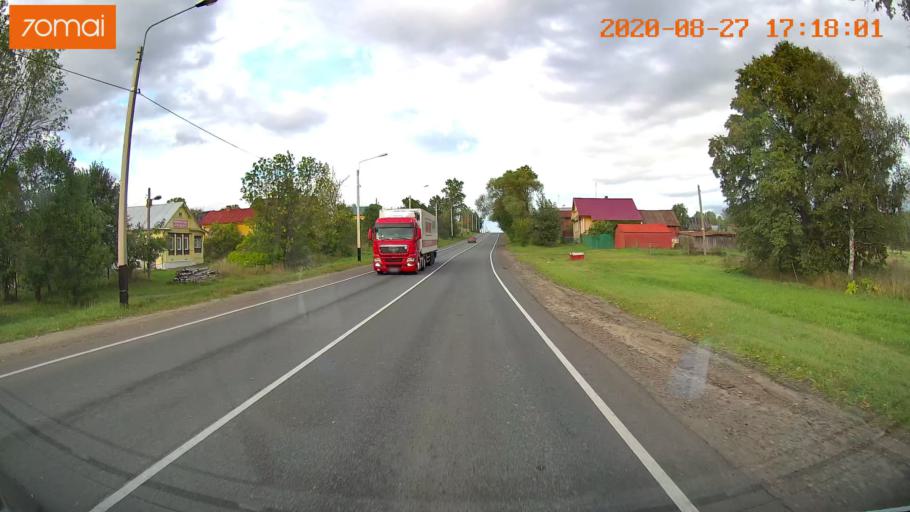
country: RU
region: Ivanovo
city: Lezhnevo
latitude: 56.7613
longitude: 40.7851
